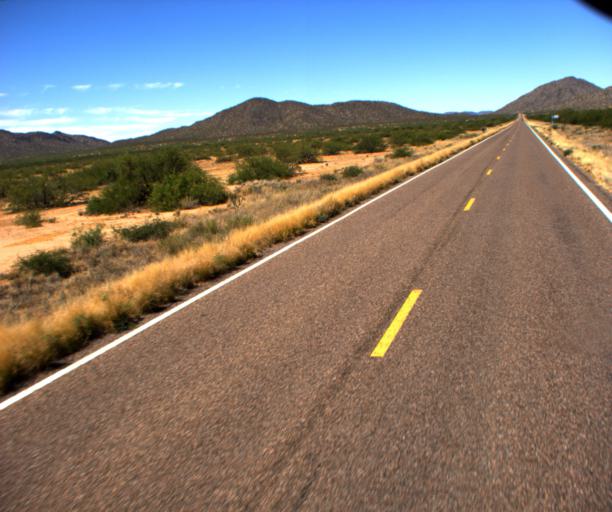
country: US
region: Arizona
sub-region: Yavapai County
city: Congress
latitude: 34.1183
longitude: -112.9634
